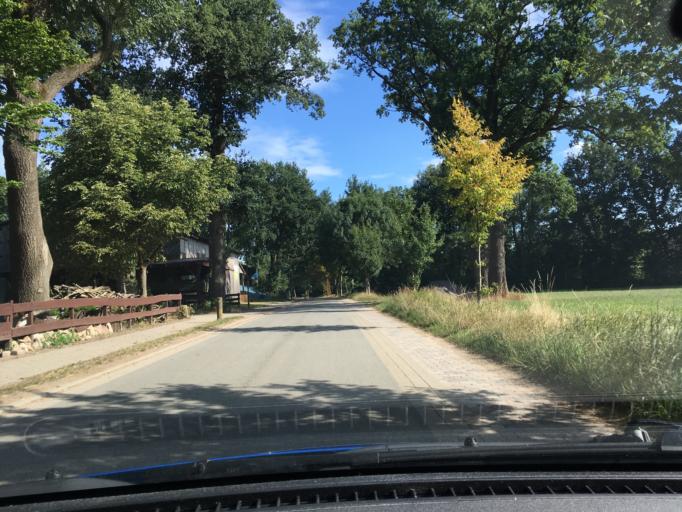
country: DE
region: Lower Saxony
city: Barum
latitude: 53.3619
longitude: 10.3919
